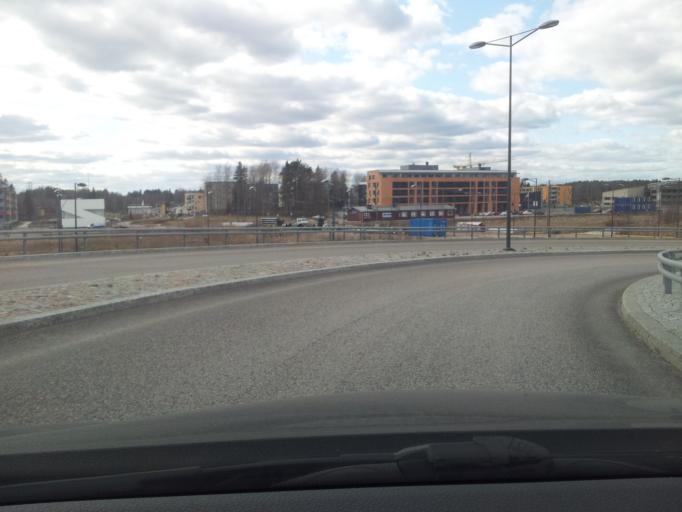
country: FI
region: Uusimaa
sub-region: Helsinki
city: Kauniainen
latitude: 60.1874
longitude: 24.7463
